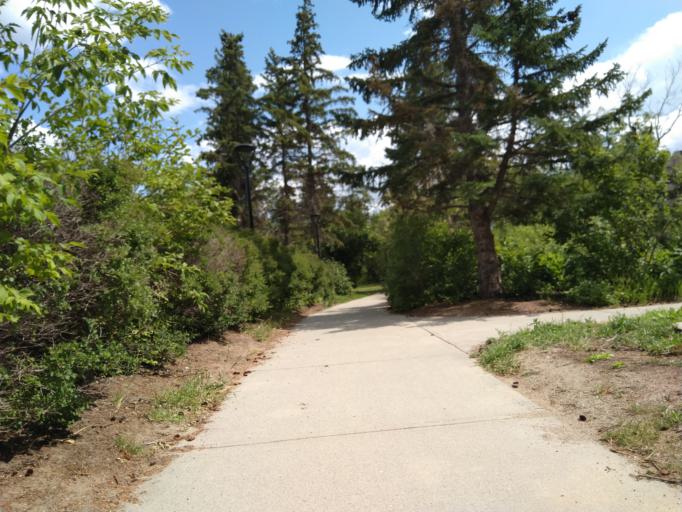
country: CA
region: Alberta
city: Calgary
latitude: 51.0816
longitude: -114.1267
